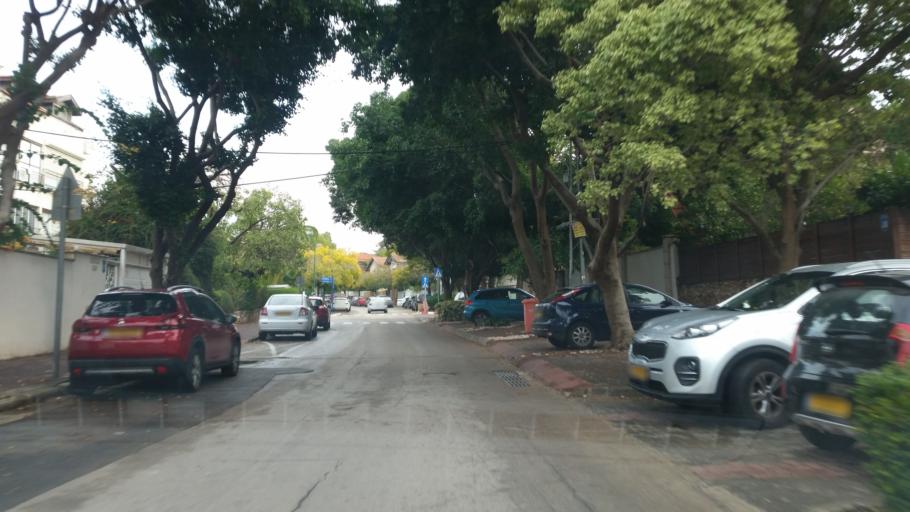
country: IL
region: Tel Aviv
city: Ramat HaSharon
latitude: 32.1578
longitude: 34.8482
